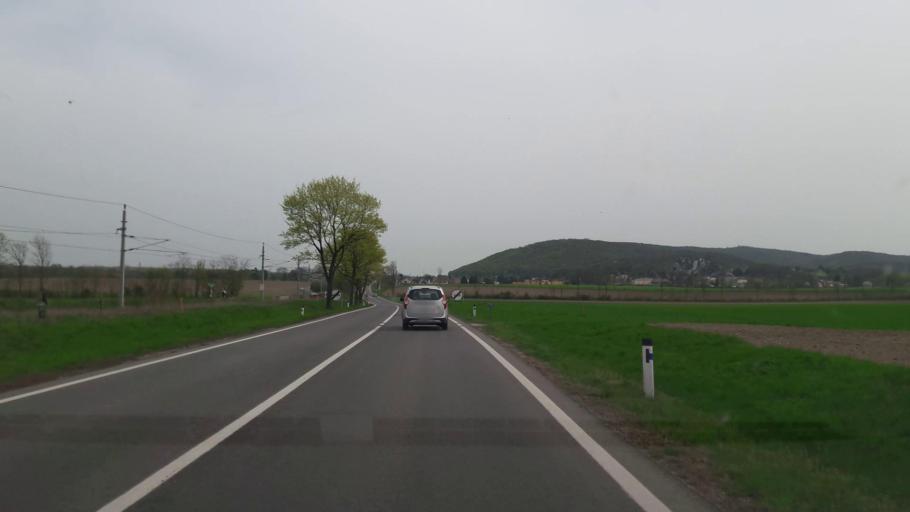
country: AT
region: Lower Austria
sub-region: Politischer Bezirk Bruck an der Leitha
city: Wolfsthal
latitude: 48.1410
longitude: 16.9895
